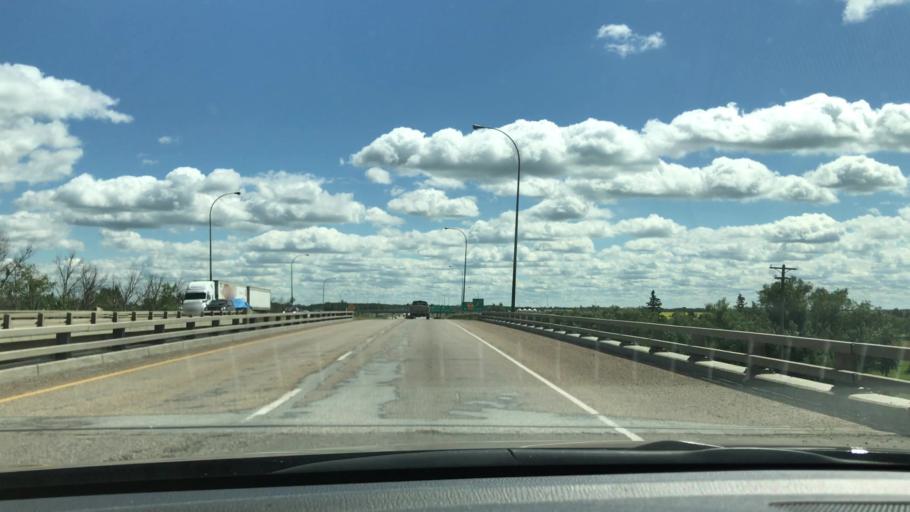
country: CA
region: Alberta
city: Leduc
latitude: 53.2582
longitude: -113.5618
